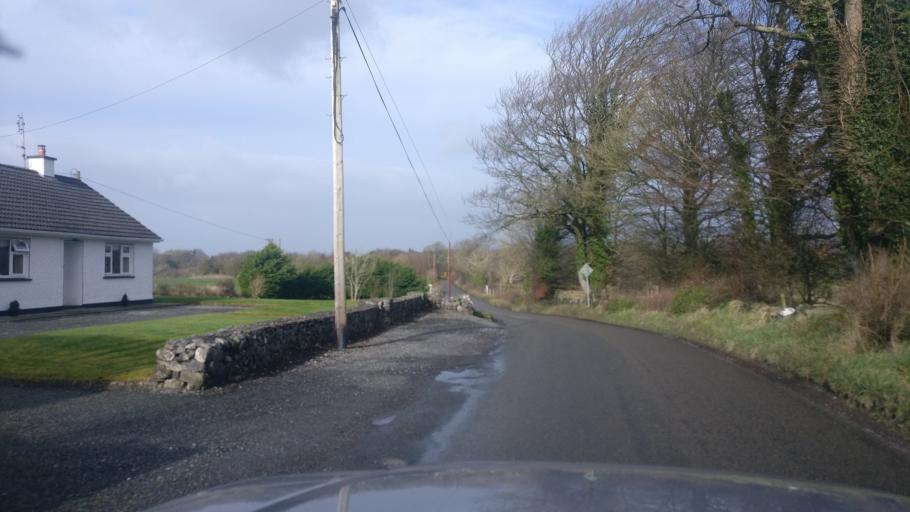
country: IE
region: Connaught
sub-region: County Galway
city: Loughrea
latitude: 53.2798
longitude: -8.5836
